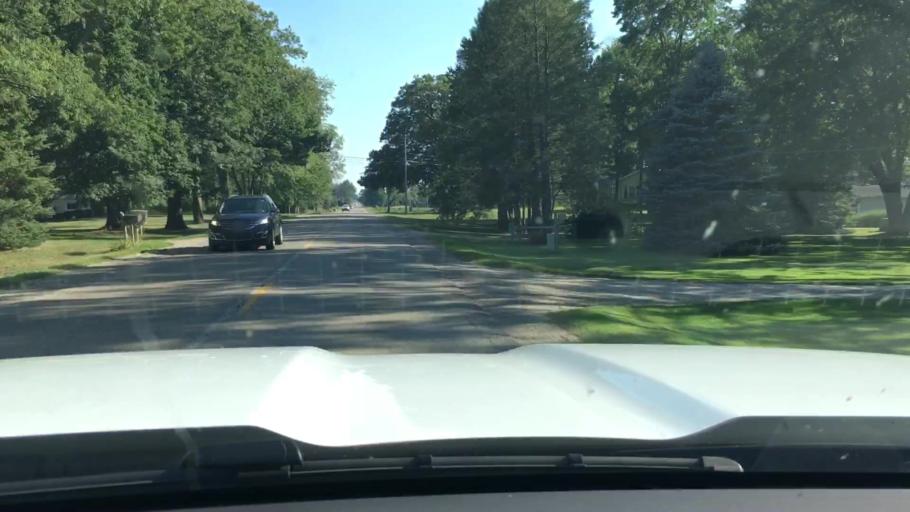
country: US
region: Michigan
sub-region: Ottawa County
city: Zeeland
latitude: 42.8792
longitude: -85.9608
